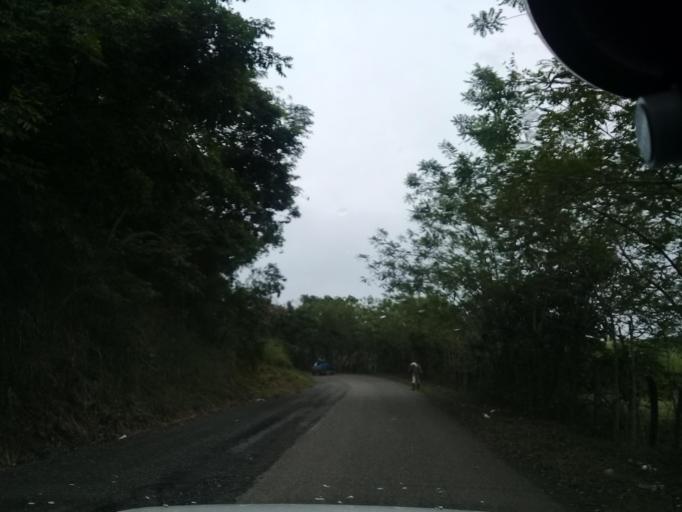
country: MX
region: Veracruz
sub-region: Chalma
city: San Pedro Coyutla
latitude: 21.2087
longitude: -98.3868
